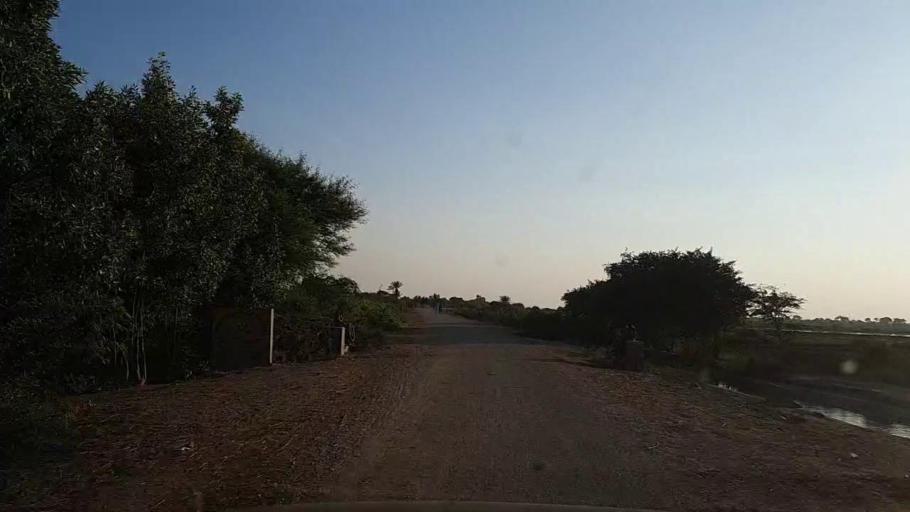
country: PK
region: Sindh
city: Thatta
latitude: 24.6234
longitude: 67.9141
